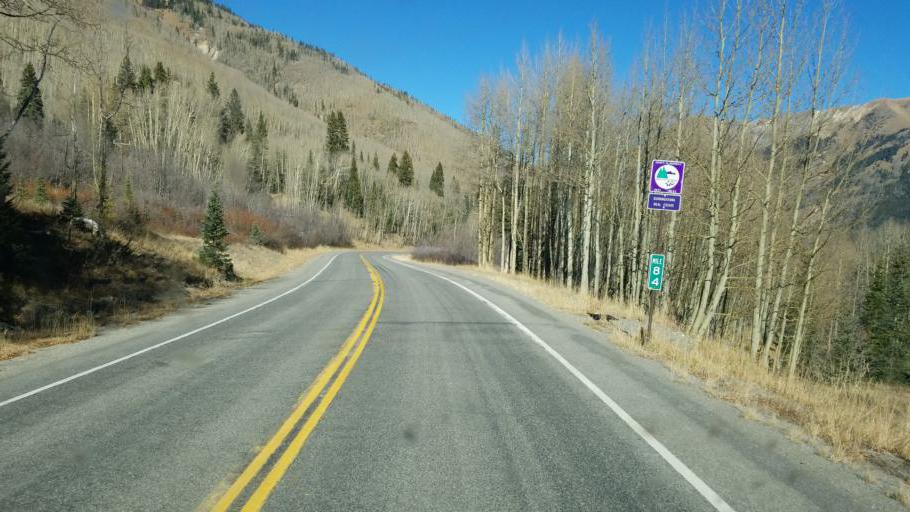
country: US
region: Colorado
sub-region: Ouray County
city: Ouray
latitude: 37.9274
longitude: -107.6910
